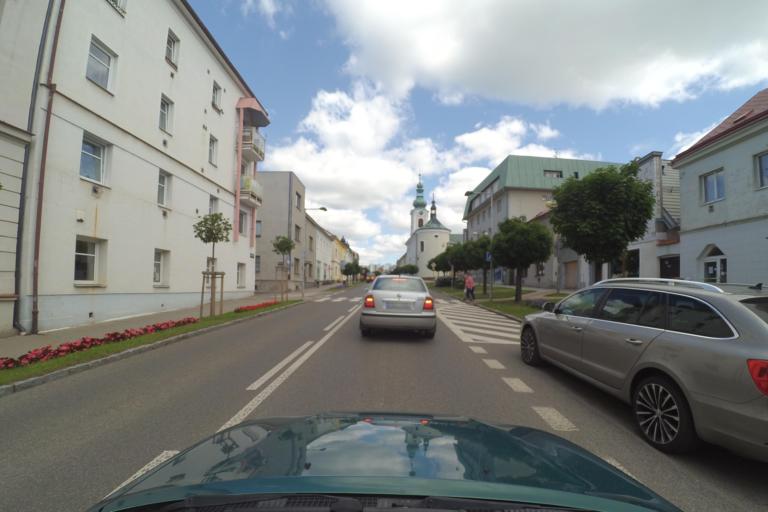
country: CZ
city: Nove Mesto nad Metuji
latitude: 50.3476
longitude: 16.1505
